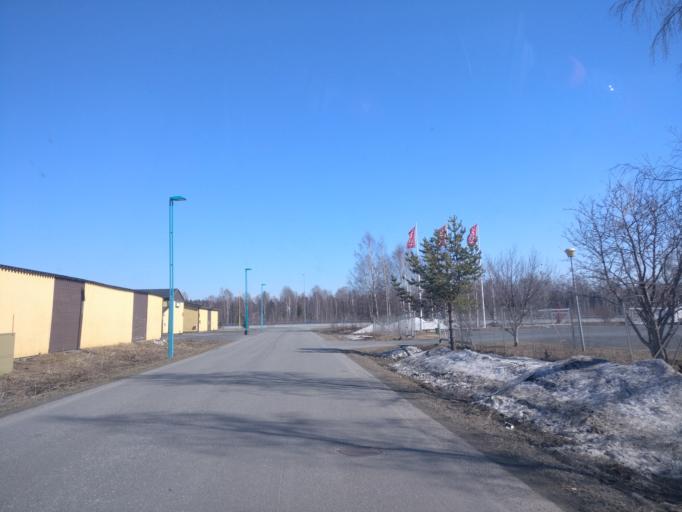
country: FI
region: Lapland
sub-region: Kemi-Tornio
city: Kemi
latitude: 65.7364
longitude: 24.5858
